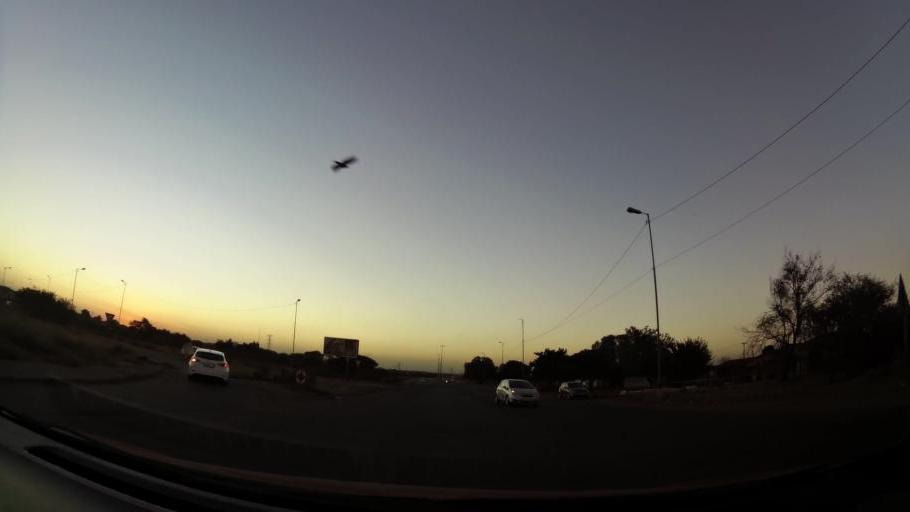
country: ZA
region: North-West
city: Ga-Rankuwa
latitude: -25.6015
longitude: 27.9922
